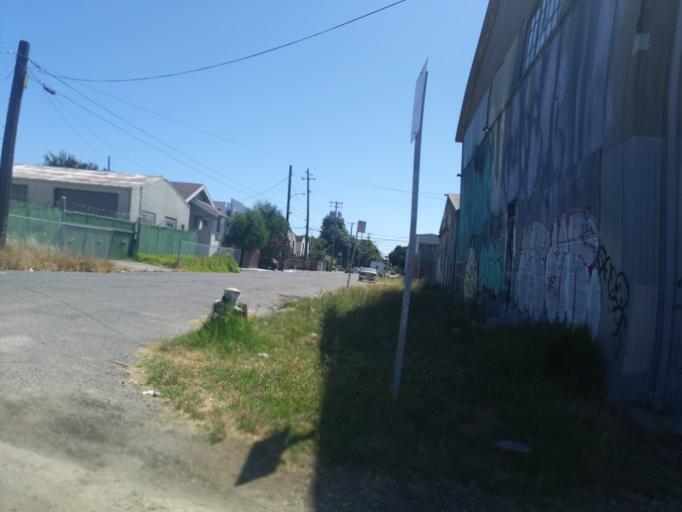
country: US
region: California
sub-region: Alameda County
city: Emeryville
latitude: 37.8147
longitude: -122.2950
